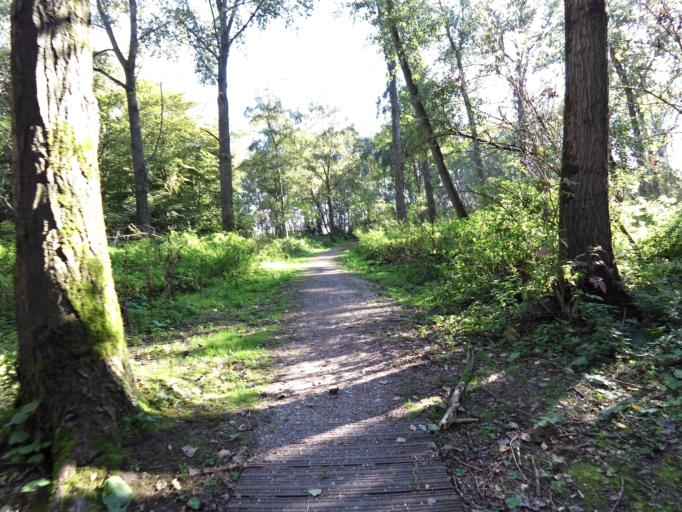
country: NL
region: South Holland
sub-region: Gemeente Vlaardingen
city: Vlaardingen
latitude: 51.9245
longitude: 4.3165
